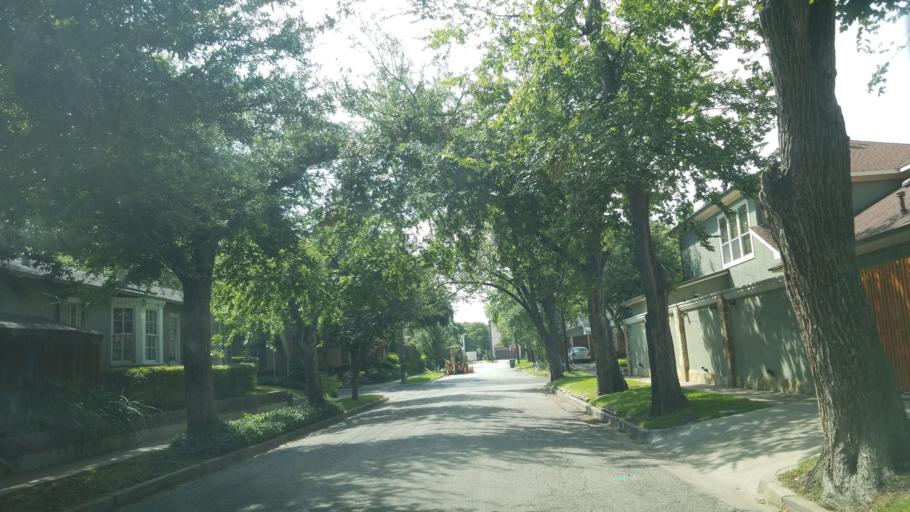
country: US
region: Texas
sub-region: Dallas County
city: Highland Park
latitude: 32.8169
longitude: -96.7844
